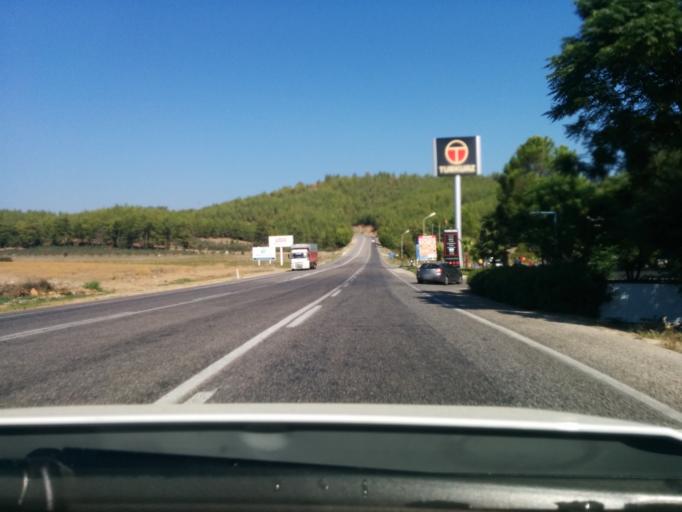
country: TR
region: Mugla
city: Kemer
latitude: 36.6125
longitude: 29.3581
